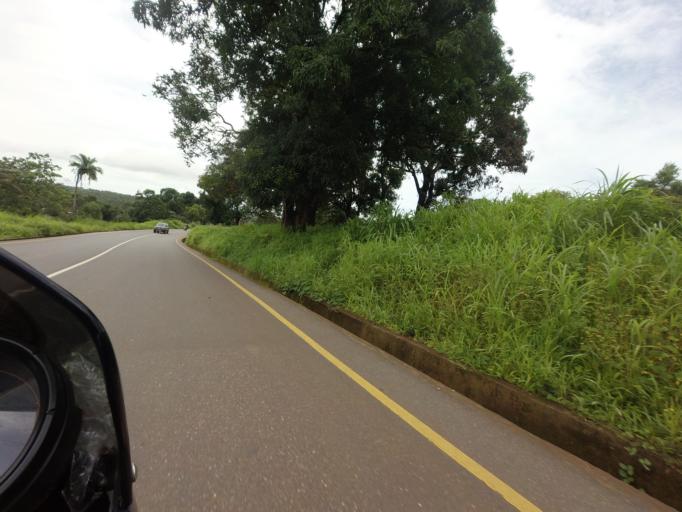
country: SL
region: Northern Province
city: Kambia
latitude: 9.1161
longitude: -12.9231
